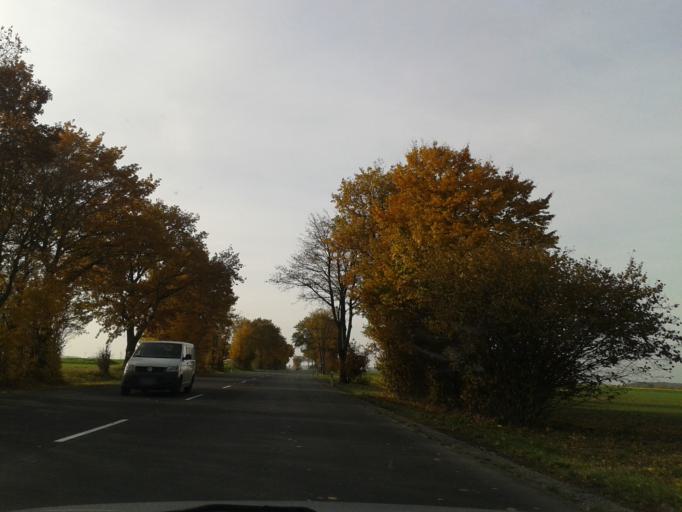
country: DE
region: North Rhine-Westphalia
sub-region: Regierungsbezirk Arnsberg
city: Ruthen
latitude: 51.5411
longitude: 8.4830
